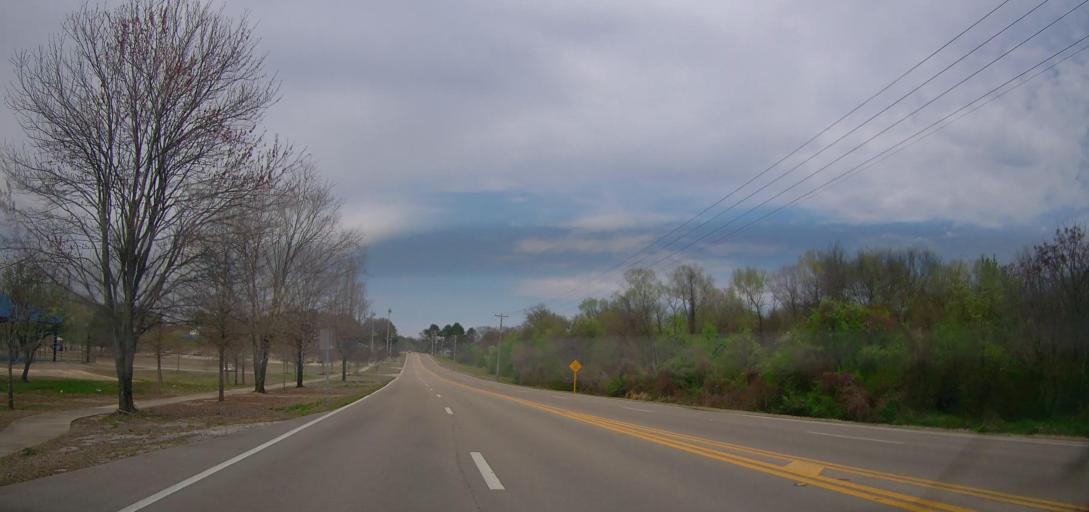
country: US
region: Mississippi
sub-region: Lee County
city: Tupelo
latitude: 34.2654
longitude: -88.7036
